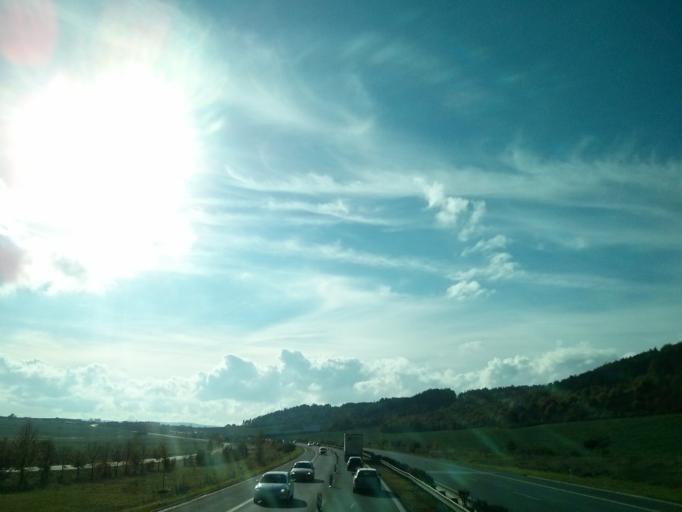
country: CZ
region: Central Bohemia
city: Zebrak
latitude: 49.8891
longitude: 13.9261
